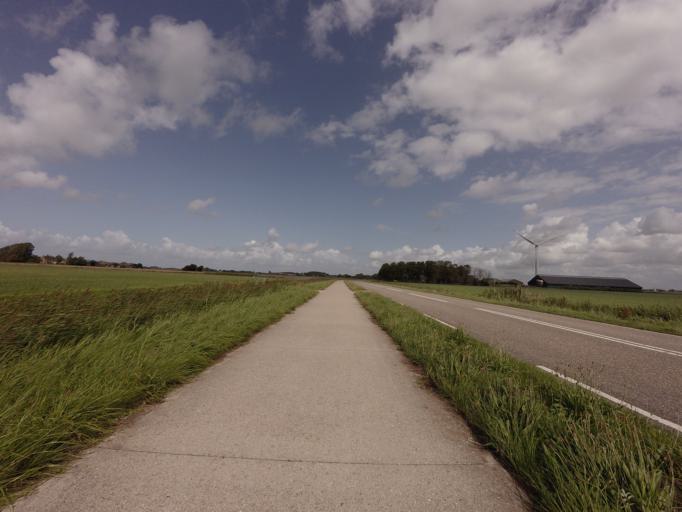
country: NL
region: Friesland
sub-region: Gemeente Harlingen
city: Harlingen
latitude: 53.1377
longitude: 5.4733
